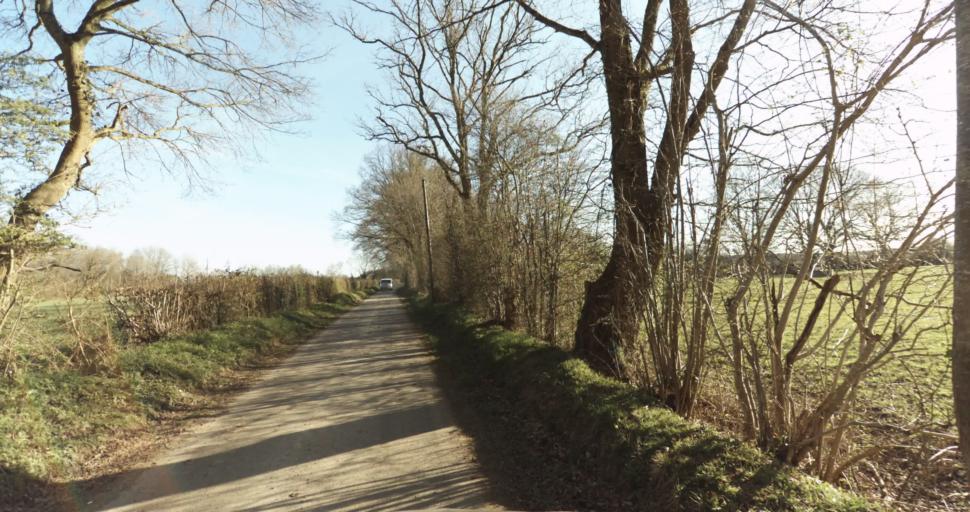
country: FR
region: Lower Normandy
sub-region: Departement du Calvados
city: Livarot
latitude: 48.9851
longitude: 0.0861
